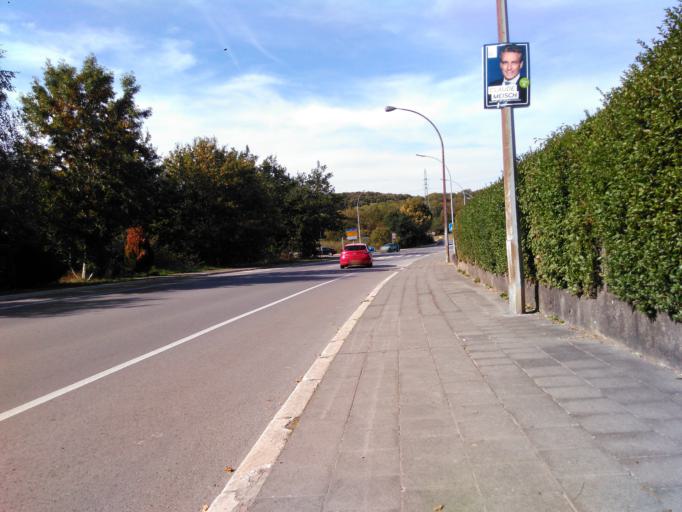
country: LU
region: Luxembourg
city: Belvaux
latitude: 49.5214
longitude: 5.9242
